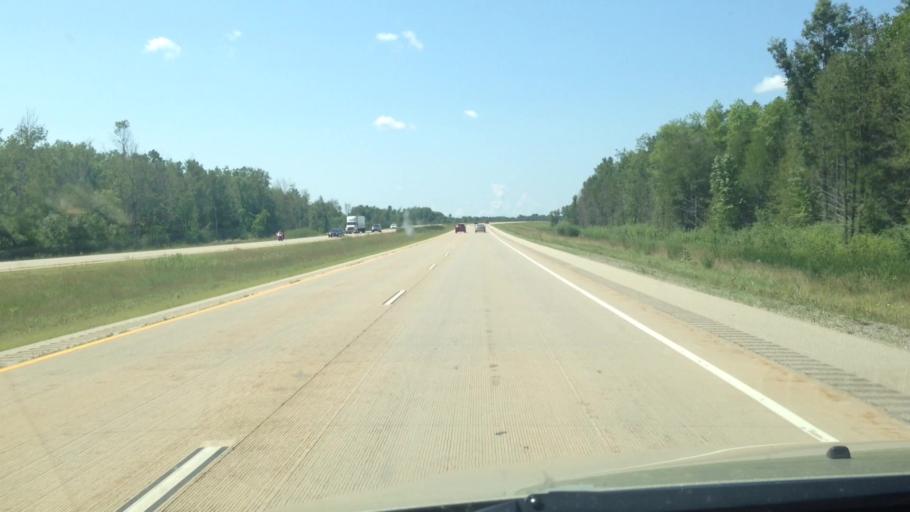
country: US
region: Wisconsin
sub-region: Oconto County
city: Oconto
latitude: 44.9135
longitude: -87.8781
